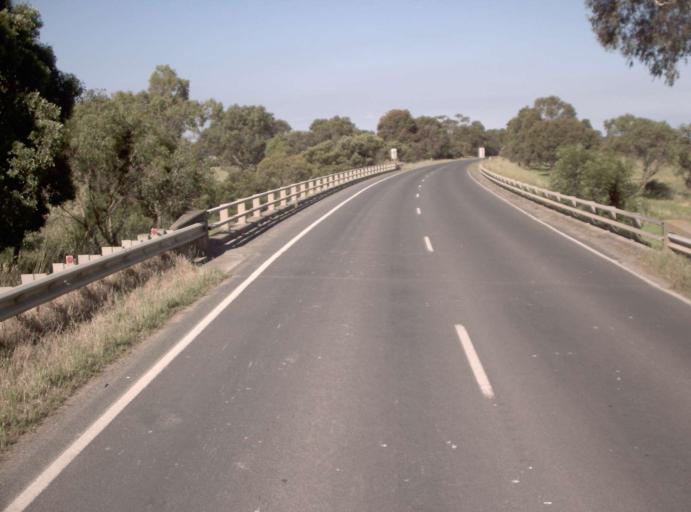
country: AU
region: Victoria
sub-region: Latrobe
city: Traralgon
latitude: -38.5507
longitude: 146.6837
